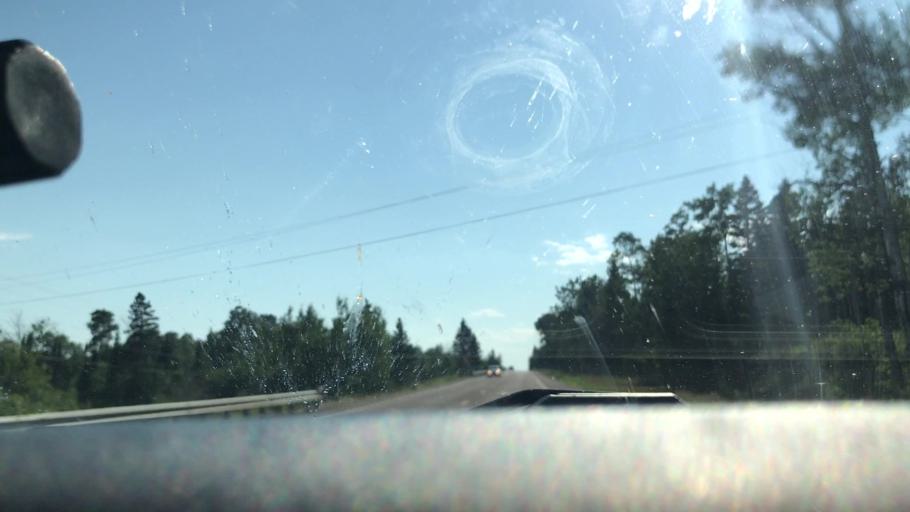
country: US
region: Minnesota
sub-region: Cook County
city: Grand Marais
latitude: 47.8252
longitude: -90.0196
